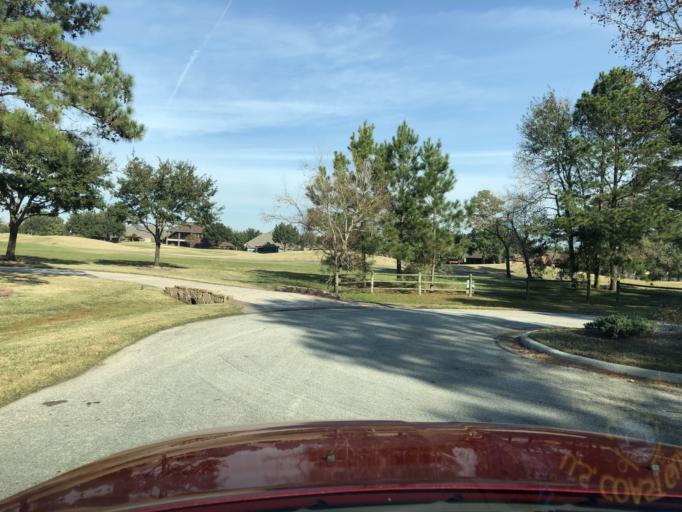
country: US
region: Texas
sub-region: Harris County
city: Tomball
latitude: 30.0443
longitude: -95.5619
